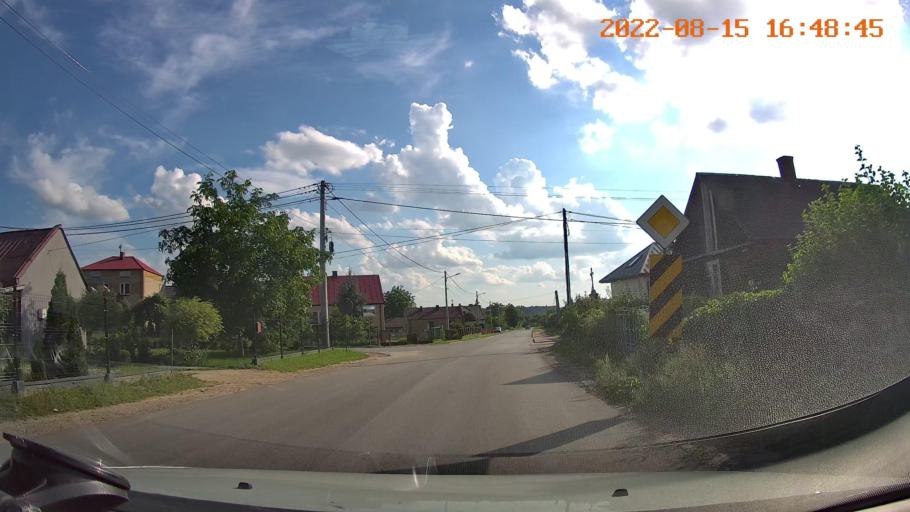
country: PL
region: Swietokrzyskie
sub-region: Powiat kielecki
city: Piekoszow
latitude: 50.8803
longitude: 20.4602
